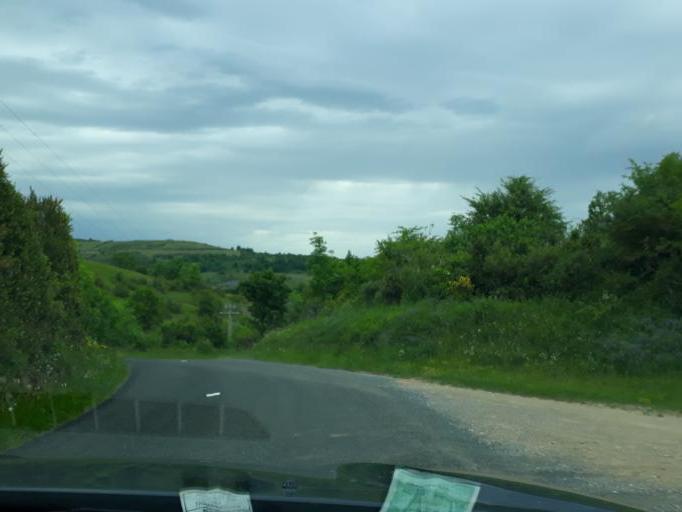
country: FR
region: Languedoc-Roussillon
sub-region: Departement de l'Herault
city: Lodeve
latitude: 43.8163
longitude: 3.2688
